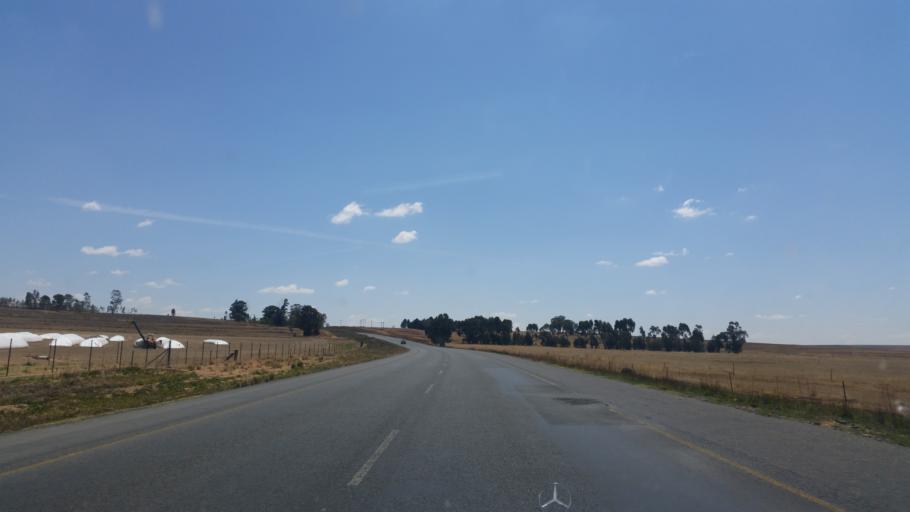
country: ZA
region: Orange Free State
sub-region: Thabo Mofutsanyana District Municipality
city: Bethlehem
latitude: -28.1190
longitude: 28.6805
